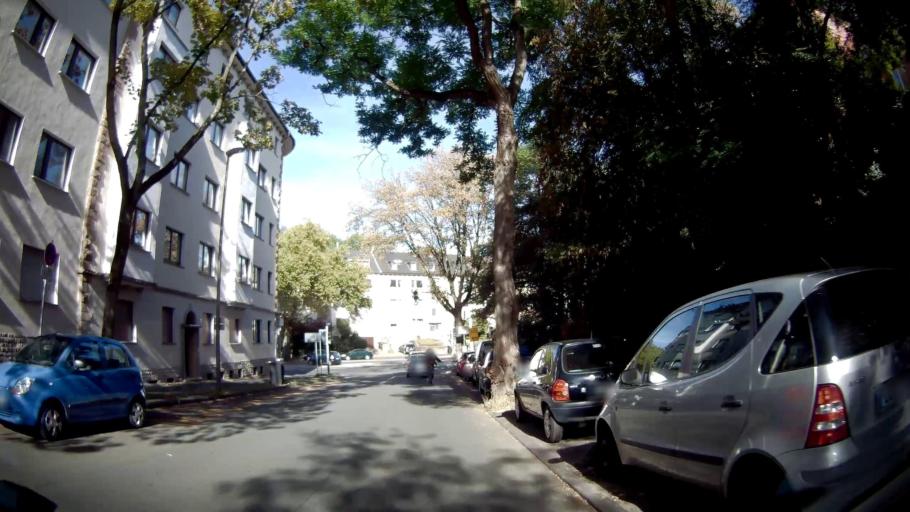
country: DE
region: North Rhine-Westphalia
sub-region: Regierungsbezirk Arnsberg
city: Bochum
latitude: 51.4680
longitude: 7.2092
